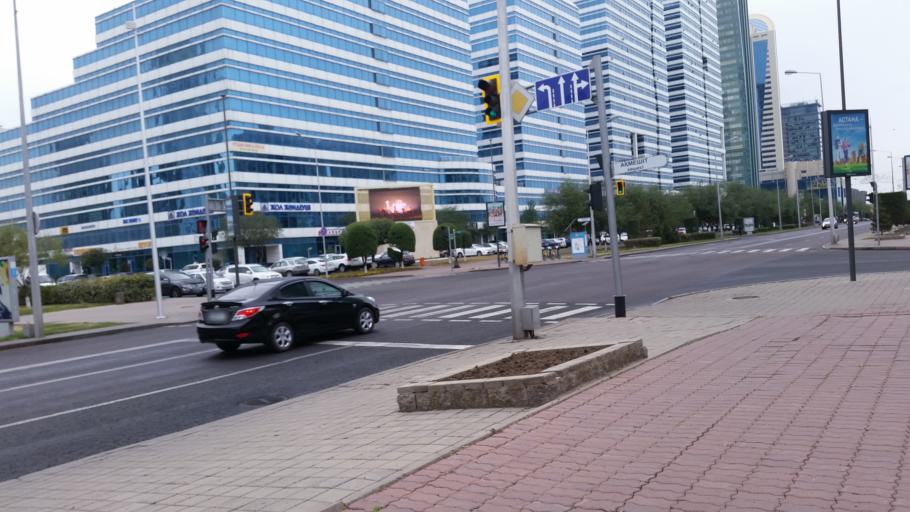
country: KZ
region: Astana Qalasy
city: Astana
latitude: 51.1309
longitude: 71.4300
